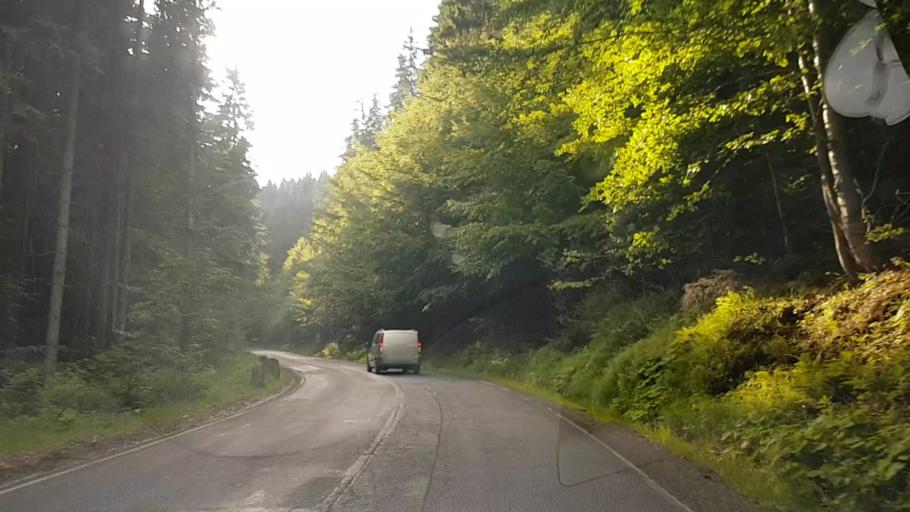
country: RO
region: Harghita
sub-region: Comuna Varsag
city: Varsag
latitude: 46.6652
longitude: 25.3133
